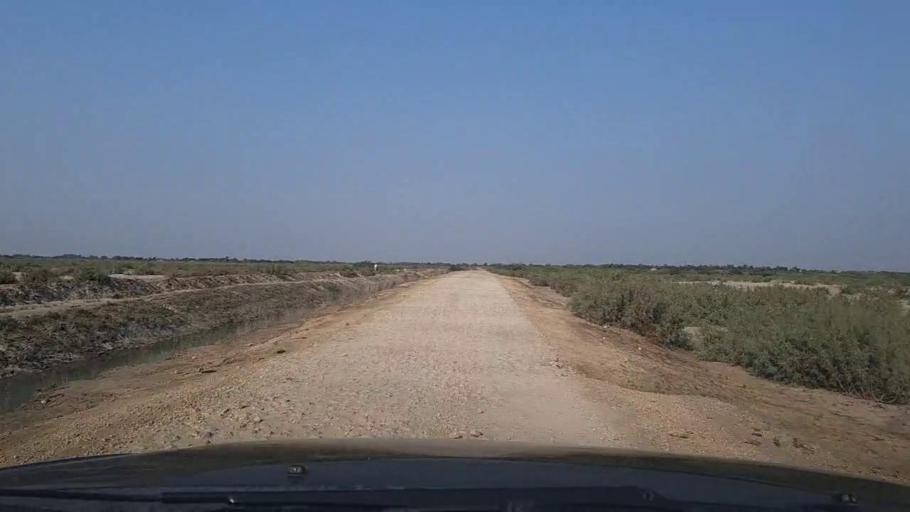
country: PK
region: Sindh
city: Mirpur Sakro
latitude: 24.6475
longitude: 67.7546
